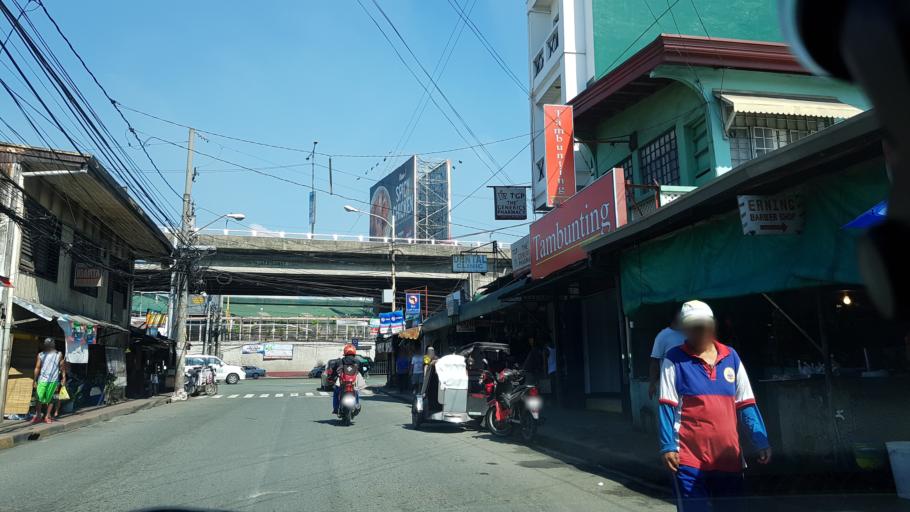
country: PH
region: Calabarzon
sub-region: Province of Rizal
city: Pateros
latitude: 14.5630
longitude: 121.0696
